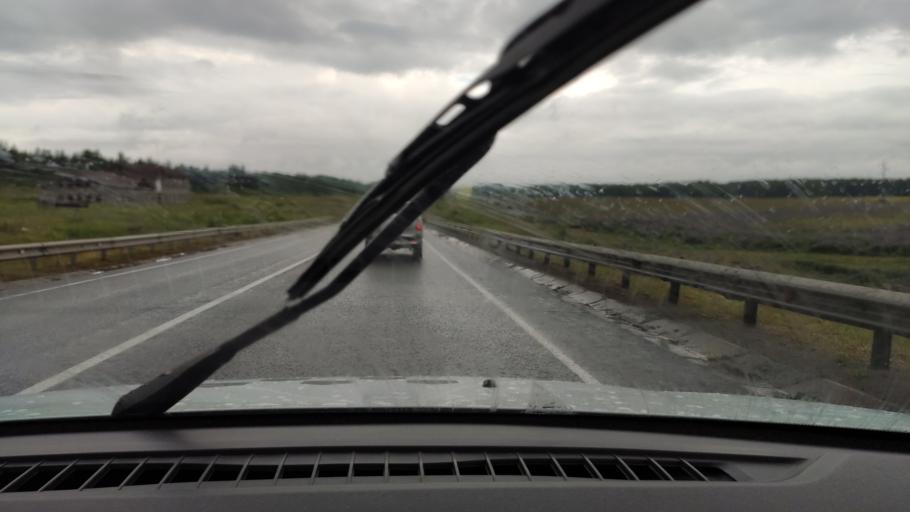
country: RU
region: Udmurtiya
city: Votkinsk
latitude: 56.9701
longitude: 53.7298
